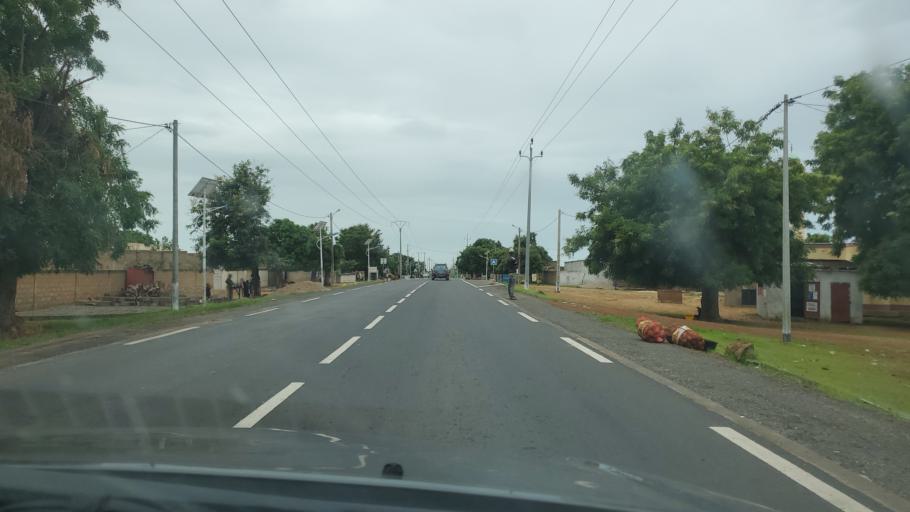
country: SN
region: Thies
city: Kayar
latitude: 15.0594
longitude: -16.9415
